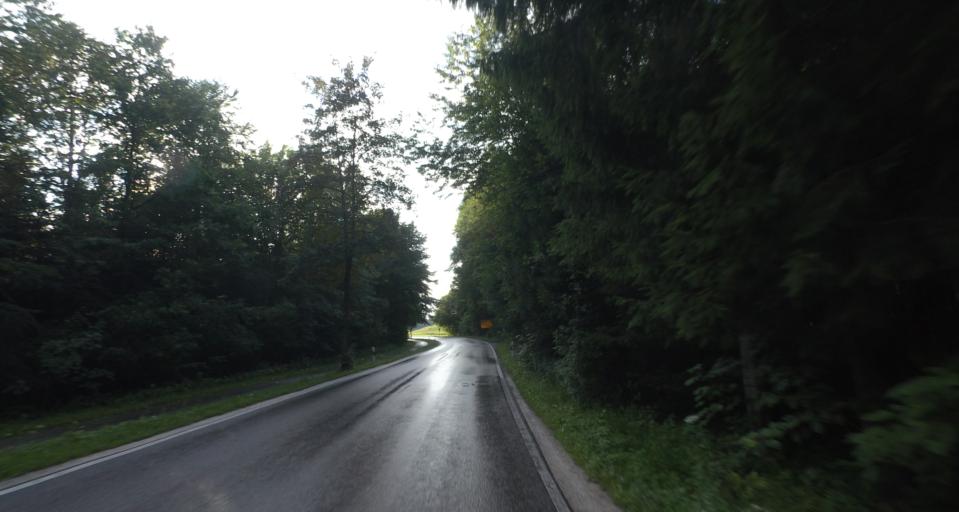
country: DE
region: Bavaria
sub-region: Upper Bavaria
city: Nussdorf
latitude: 47.9145
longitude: 12.5718
